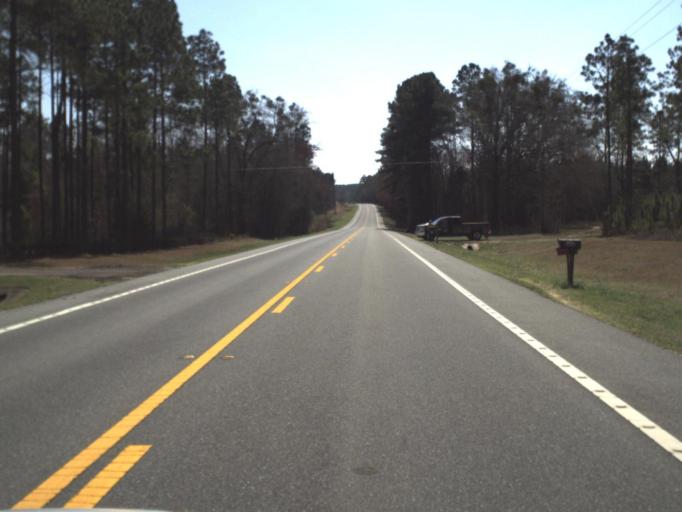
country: US
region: Florida
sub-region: Jackson County
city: Sneads
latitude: 30.6155
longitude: -85.0297
